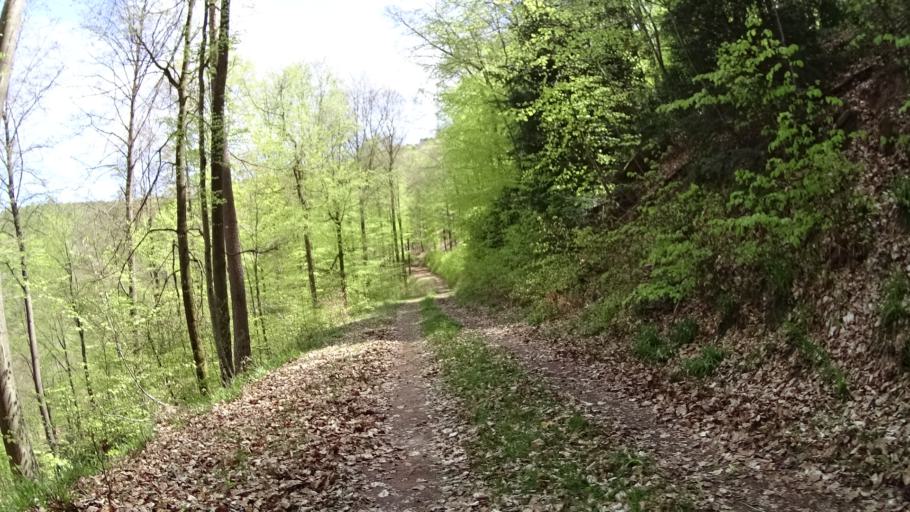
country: DE
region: Rheinland-Pfalz
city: Ramberg
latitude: 49.3108
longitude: 8.0072
